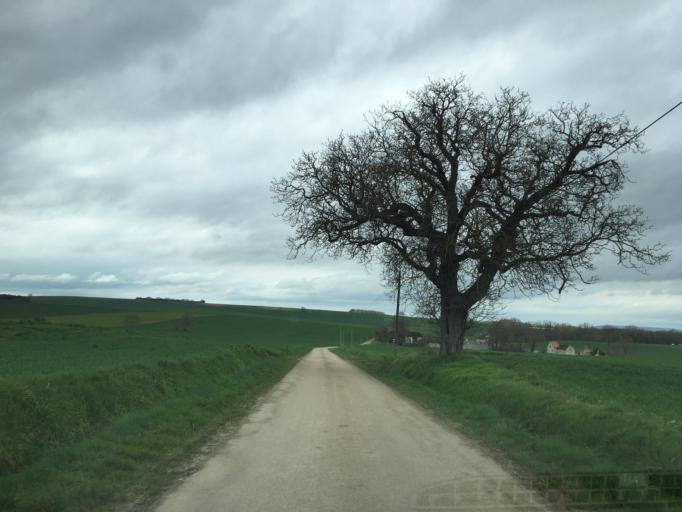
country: FR
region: Bourgogne
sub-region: Departement de l'Yonne
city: Fleury-la-Vallee
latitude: 47.8474
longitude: 3.4382
